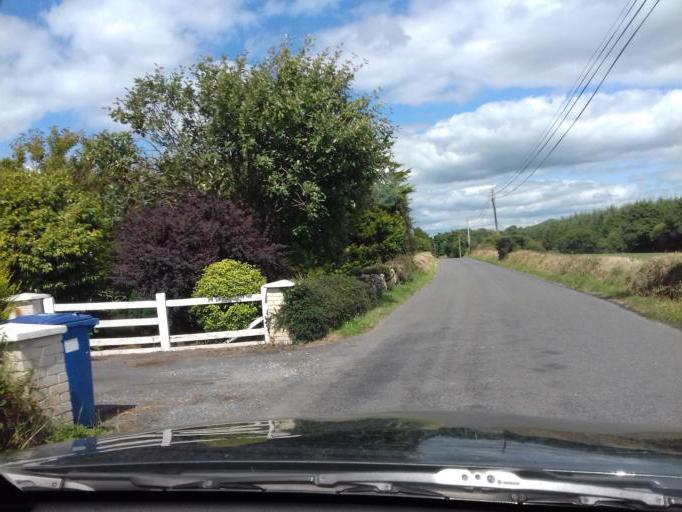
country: IE
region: Munster
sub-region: Waterford
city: Tra Mhor
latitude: 52.1716
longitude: -7.2372
